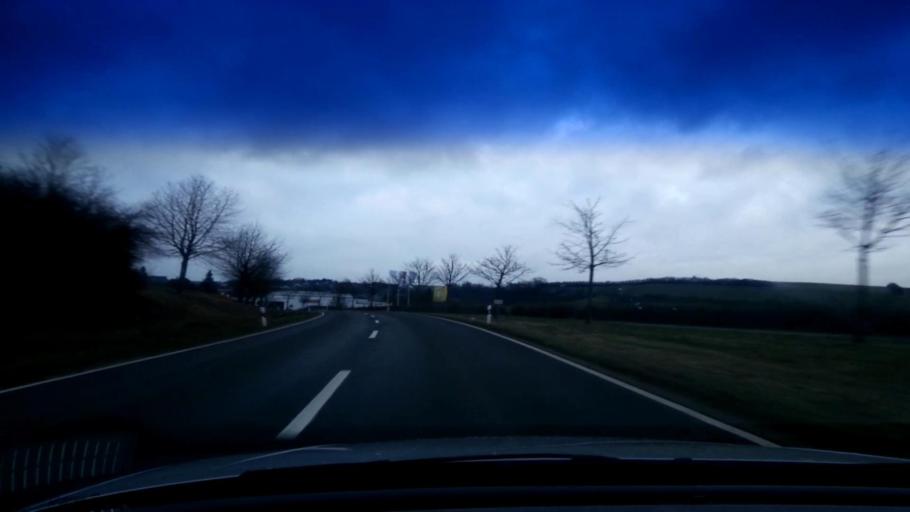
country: DE
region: Bavaria
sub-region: Upper Franconia
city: Burgebrach
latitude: 49.8555
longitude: 10.7255
